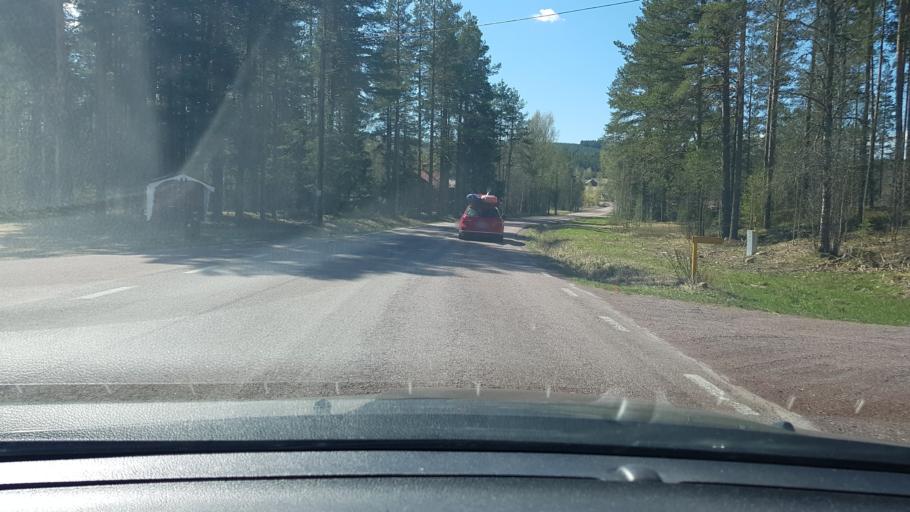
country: SE
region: Dalarna
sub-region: Alvdalens Kommun
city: AElvdalen
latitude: 61.1236
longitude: 14.1735
